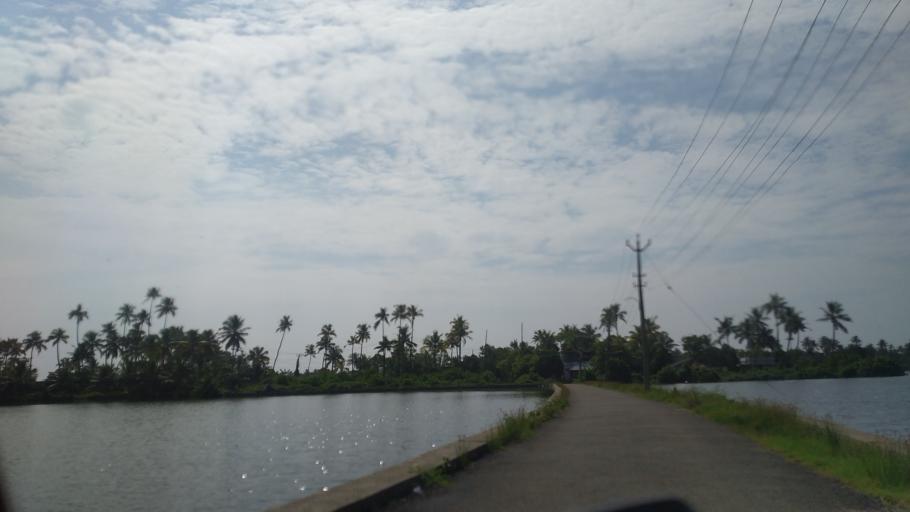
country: IN
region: Kerala
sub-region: Ernakulam
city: Elur
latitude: 10.0819
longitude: 76.1988
